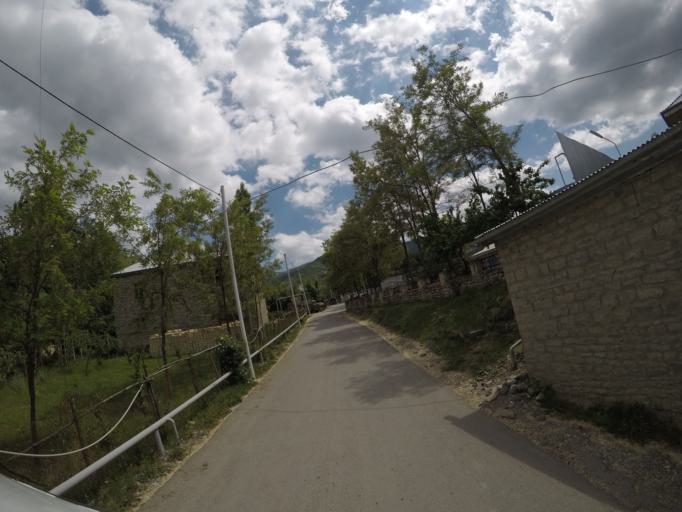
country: AZ
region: Ismayilli
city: Basqal
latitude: 40.8495
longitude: 48.3852
